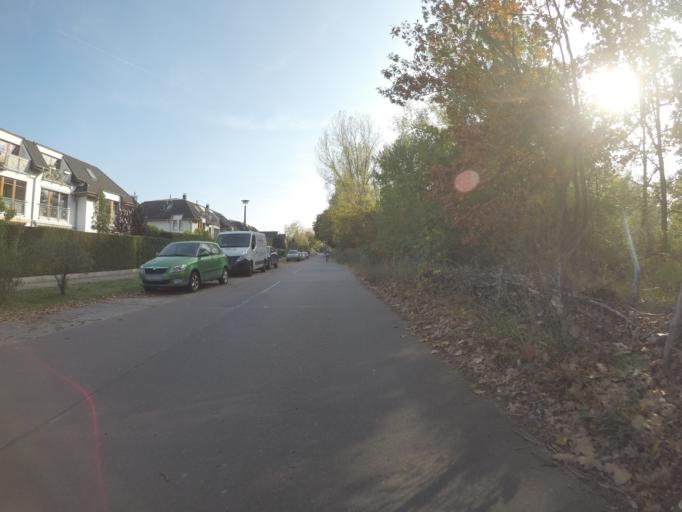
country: DE
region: Berlin
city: Altglienicke
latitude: 52.4154
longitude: 13.5416
